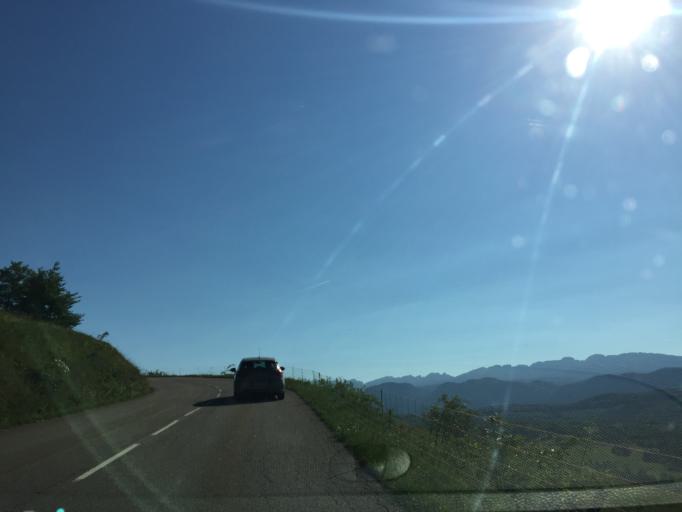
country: FR
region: Rhone-Alpes
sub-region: Departement de la Drome
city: Saint-Laurent-en-Royans
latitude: 44.9120
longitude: 5.3693
